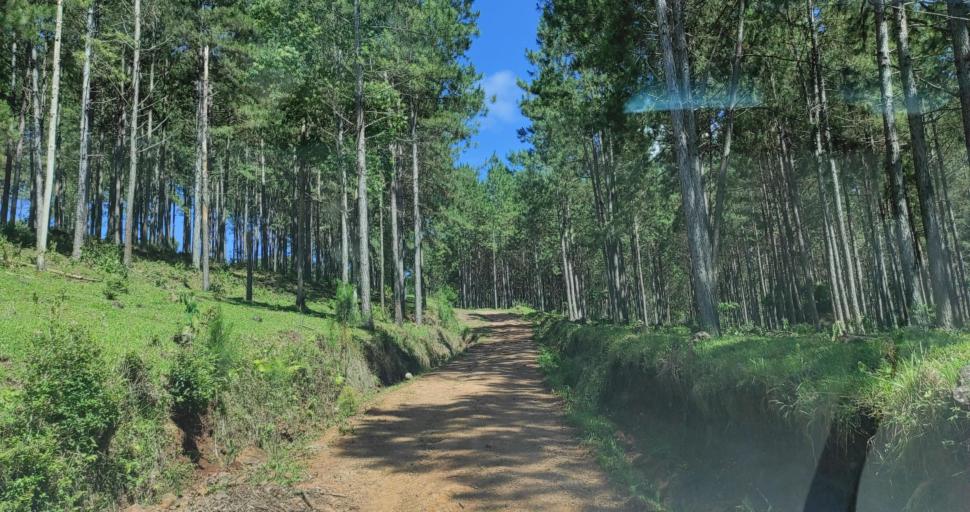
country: AR
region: Misiones
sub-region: Departamento de Veinticinco de Mayo
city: Veinticinco de Mayo
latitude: -27.4182
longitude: -54.7122
